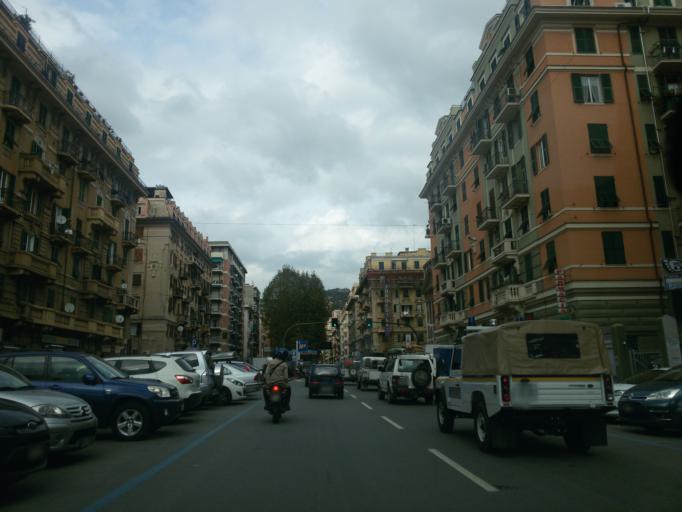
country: IT
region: Liguria
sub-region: Provincia di Genova
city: Genoa
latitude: 44.4106
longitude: 8.9547
